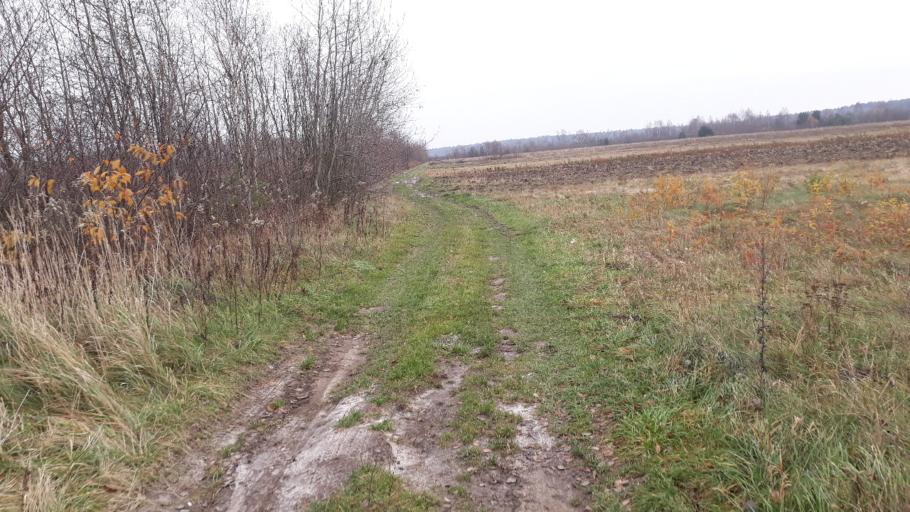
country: PL
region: Lublin Voivodeship
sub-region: Powiat janowski
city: Dzwola
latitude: 50.6598
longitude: 22.6084
